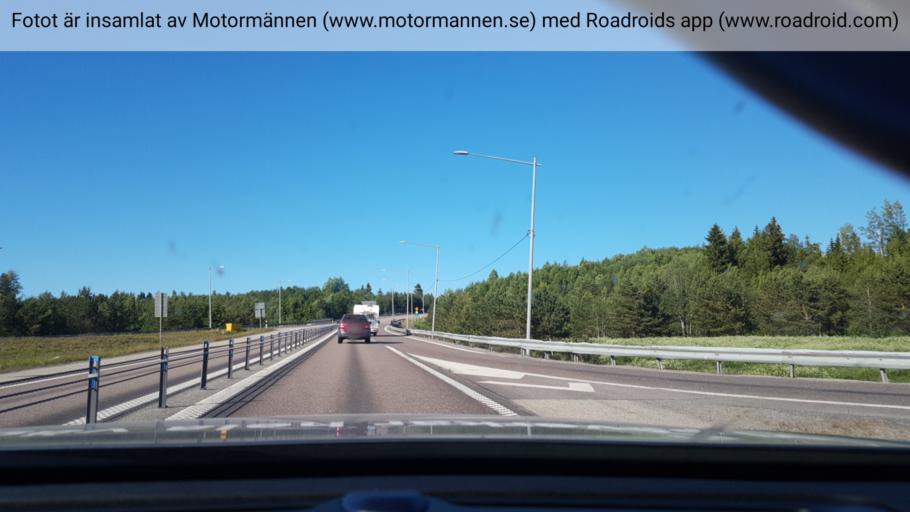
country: SE
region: Vaesternorrland
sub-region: Timra Kommun
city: Soraker
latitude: 62.5251
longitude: 17.4747
